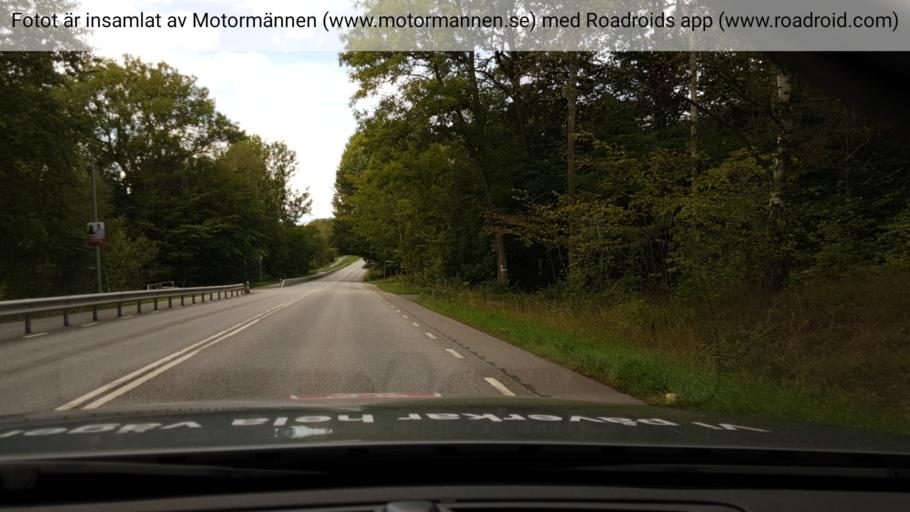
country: SE
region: Stockholm
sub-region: Upplands-Bro Kommun
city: Kungsaengen
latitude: 59.4842
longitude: 17.6985
